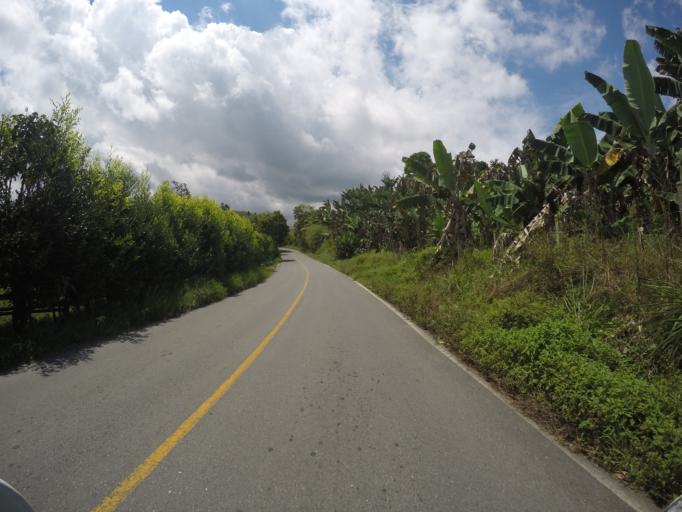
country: CO
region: Quindio
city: Filandia
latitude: 4.6464
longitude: -75.6811
